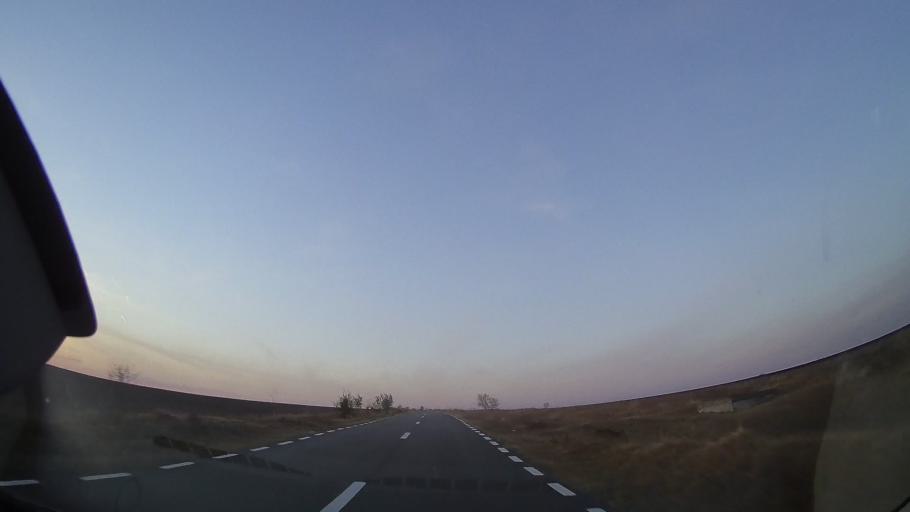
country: RO
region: Constanta
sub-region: Comuna Cobadin
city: Cobadin
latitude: 44.0245
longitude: 28.2659
